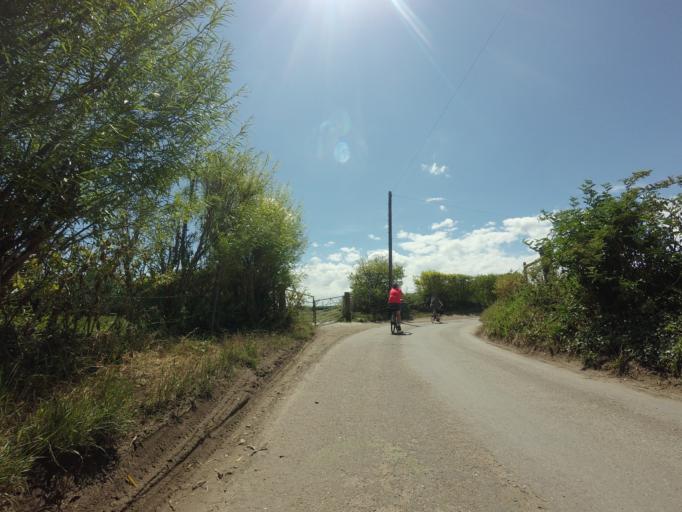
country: GB
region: England
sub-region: Medway
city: Cooling
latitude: 51.4577
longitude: 0.5138
